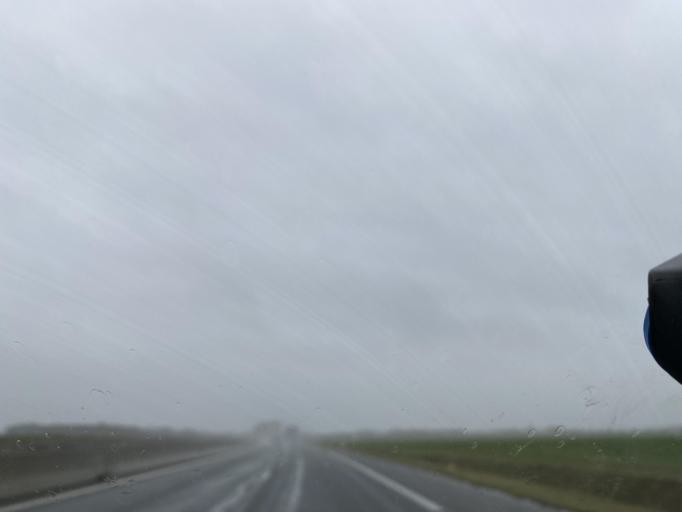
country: FR
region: Centre
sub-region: Departement d'Eure-et-Loir
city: Vernouillet
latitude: 48.6837
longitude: 1.3814
